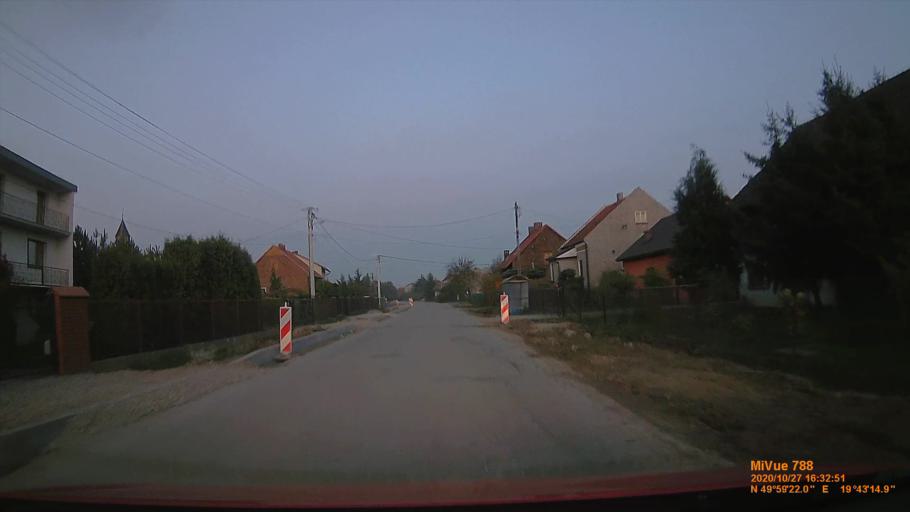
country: PL
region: Lesser Poland Voivodeship
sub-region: Powiat krakowski
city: Wolowice
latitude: 49.9894
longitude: 19.7208
